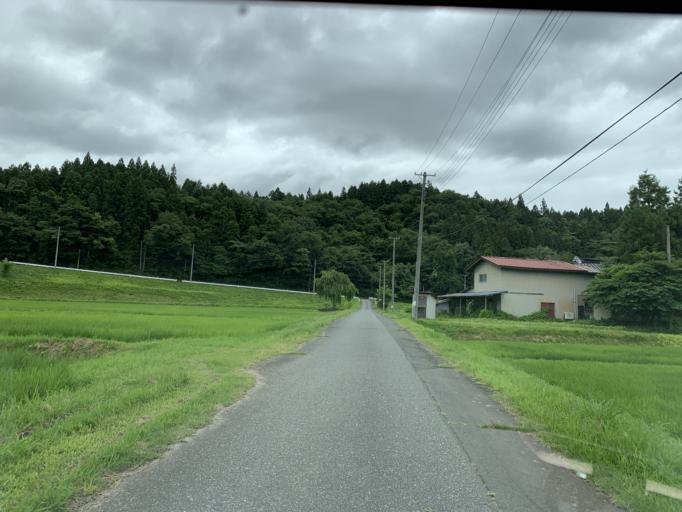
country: JP
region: Iwate
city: Ichinoseki
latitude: 38.9140
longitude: 141.0761
